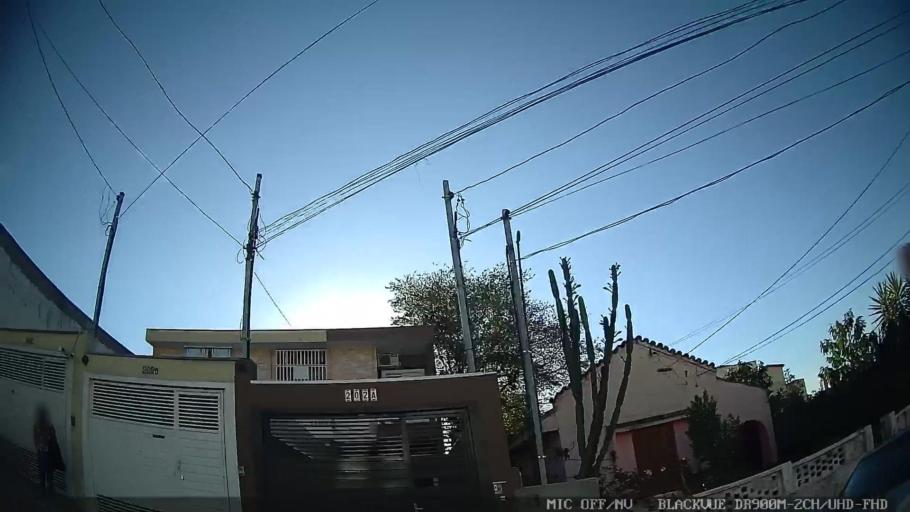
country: BR
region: Sao Paulo
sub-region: Guarulhos
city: Guarulhos
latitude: -23.5315
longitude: -46.5180
